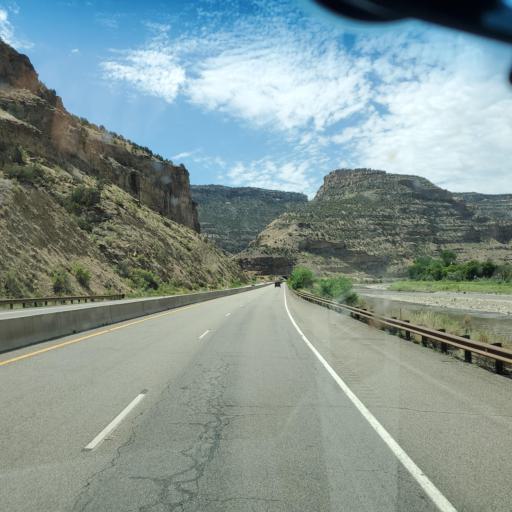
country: US
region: Colorado
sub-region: Mesa County
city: Palisade
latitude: 39.1887
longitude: -108.2805
